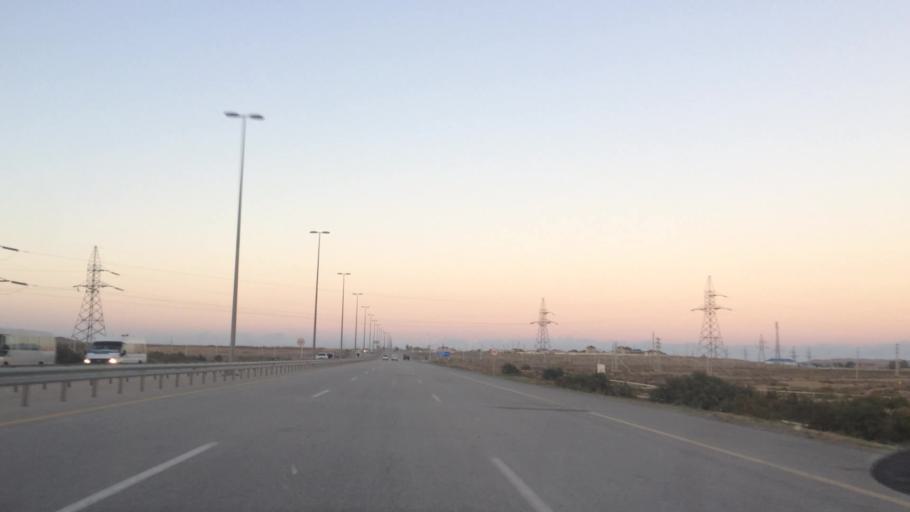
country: AZ
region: Baki
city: Qobustan
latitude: 39.9765
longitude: 49.4196
